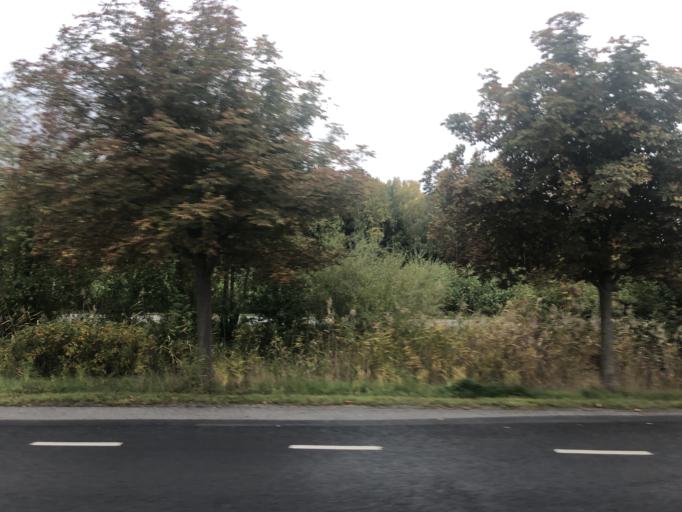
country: SE
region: Stockholm
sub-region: Jarfalla Kommun
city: Jakobsberg
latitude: 59.4190
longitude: 17.8172
